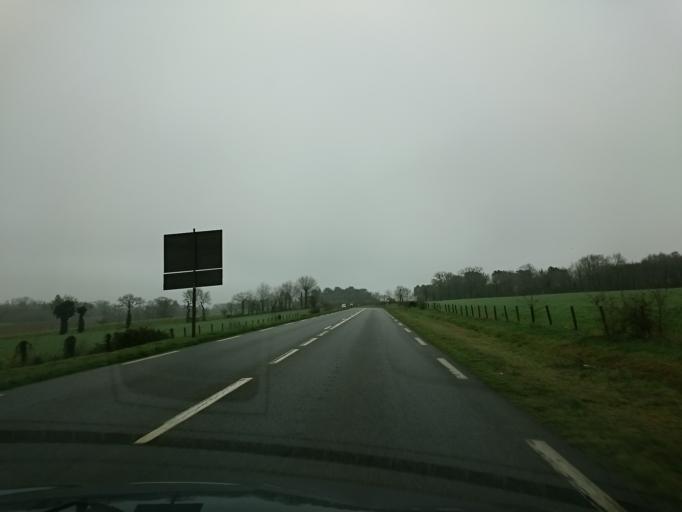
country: FR
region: Brittany
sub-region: Departement d'Ille-et-Vilaine
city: Bourg-des-Comptes
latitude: 47.9279
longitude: -1.7261
